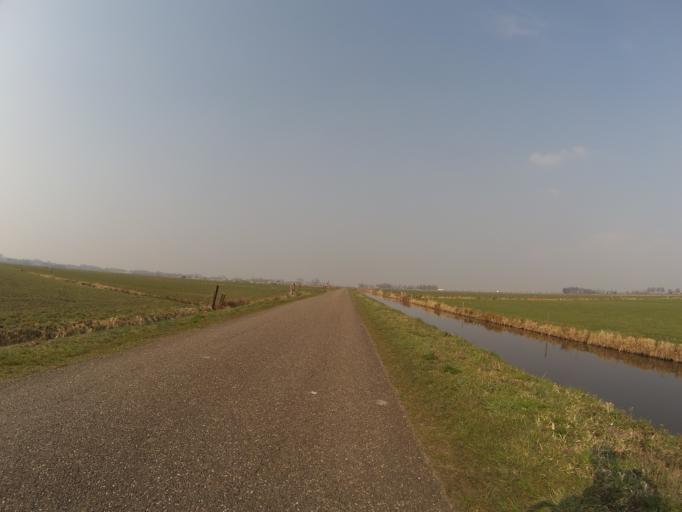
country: NL
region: Utrecht
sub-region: Gemeente Baarn
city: Baarn
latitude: 52.2058
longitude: 5.3294
